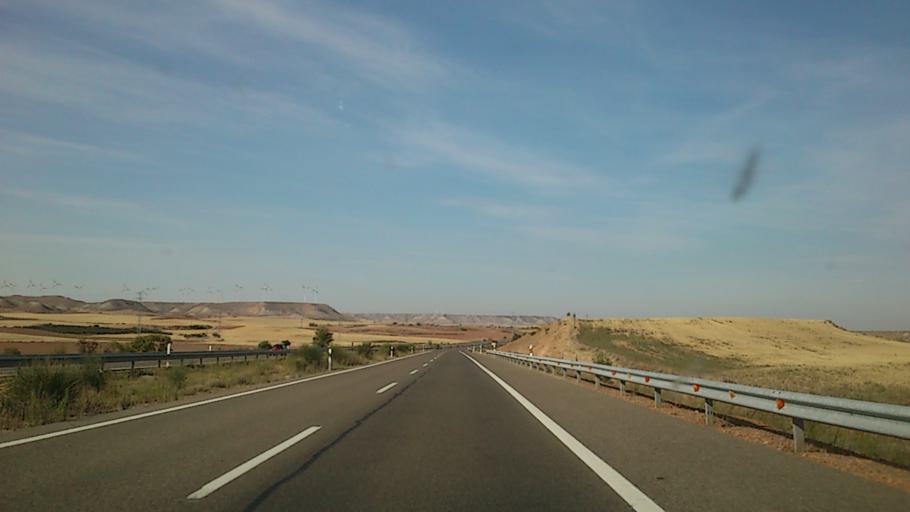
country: ES
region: Aragon
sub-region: Provincia de Zaragoza
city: Longares
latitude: 41.4364
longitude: -1.1435
